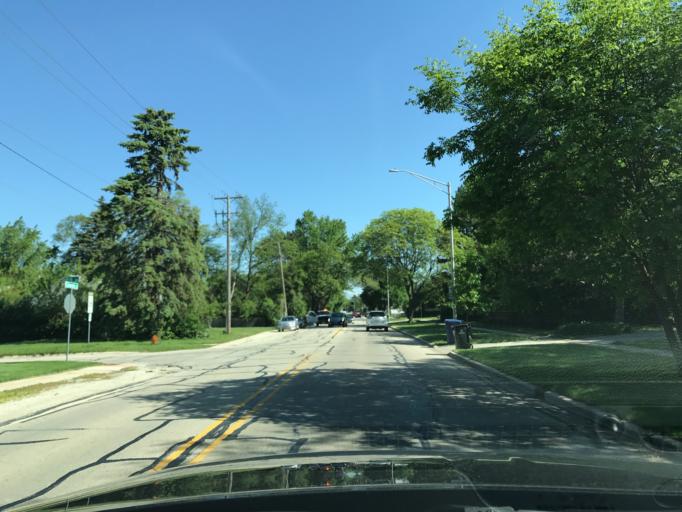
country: US
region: Illinois
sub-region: DuPage County
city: Naperville
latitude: 41.7831
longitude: -88.1371
